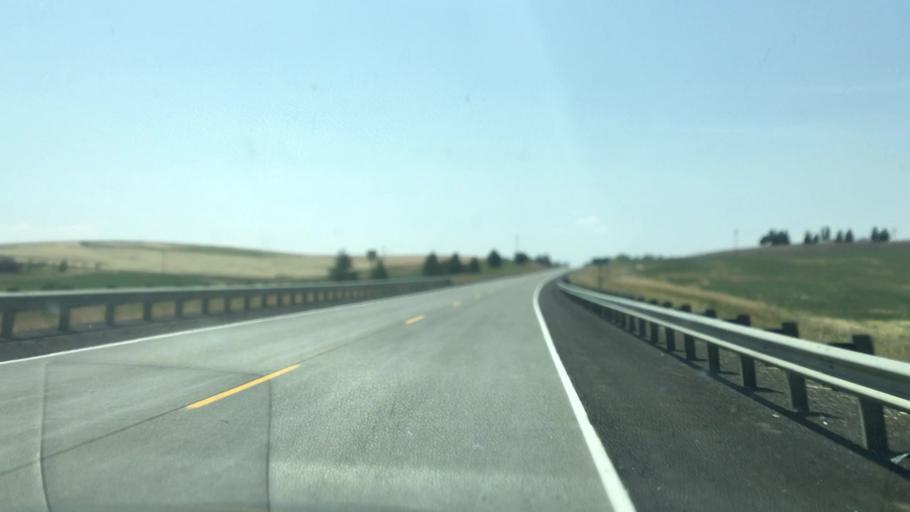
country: US
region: Idaho
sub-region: Lewis County
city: Nezperce
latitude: 46.0684
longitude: -116.3416
